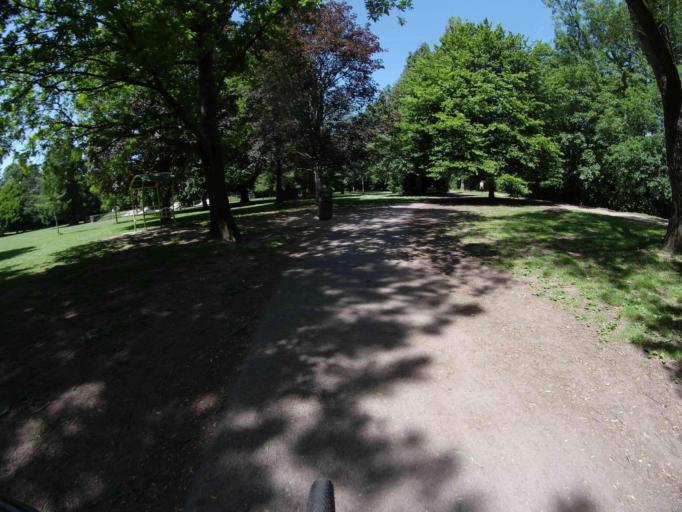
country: GB
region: England
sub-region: Devon
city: Bovey Tracey
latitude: 50.5933
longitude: -3.6783
